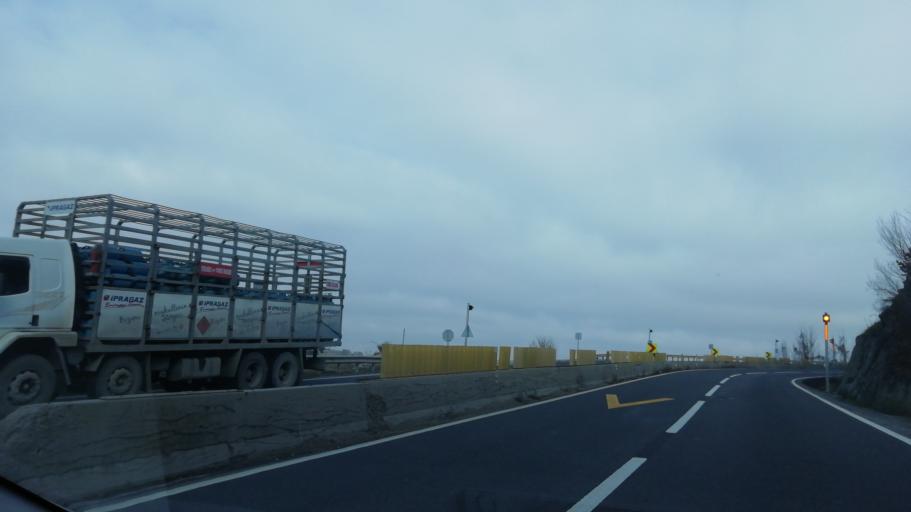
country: TR
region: Duzce
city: Kaynasli
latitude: 40.7539
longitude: 31.3884
